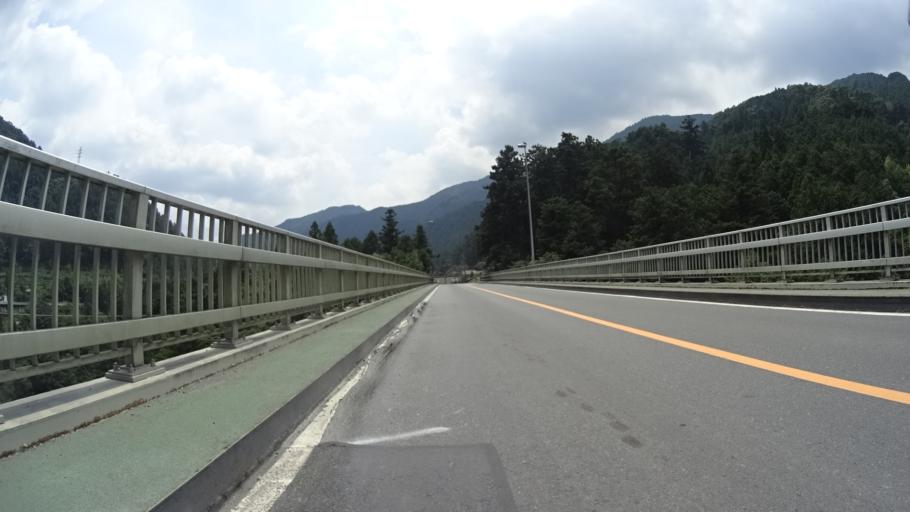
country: JP
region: Tokyo
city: Ome
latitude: 35.8146
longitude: 139.1527
